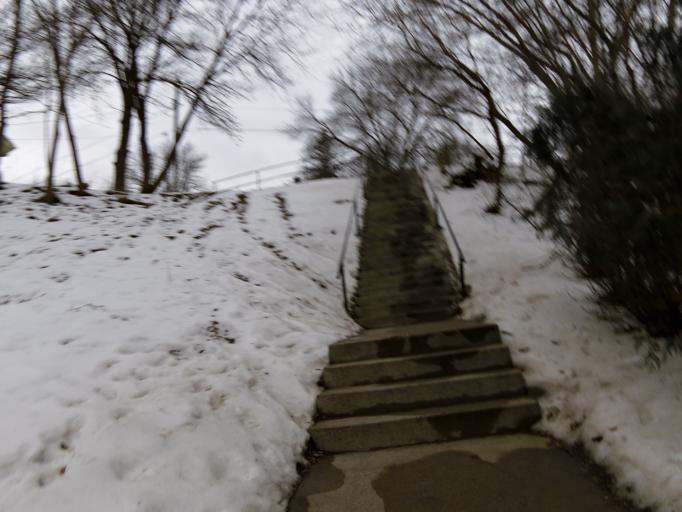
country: US
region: Minnesota
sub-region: Washington County
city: Stillwater
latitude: 45.0500
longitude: -92.8034
